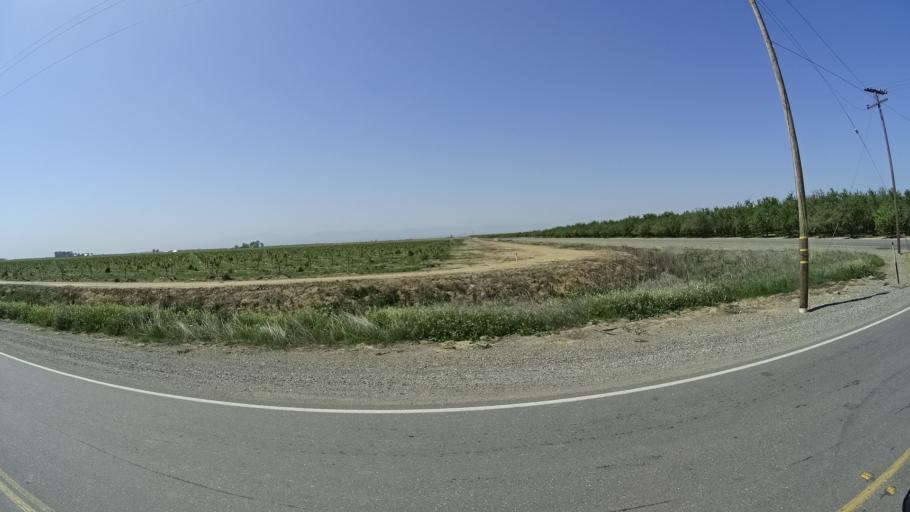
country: US
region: California
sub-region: Glenn County
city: Willows
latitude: 39.6234
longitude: -122.1376
